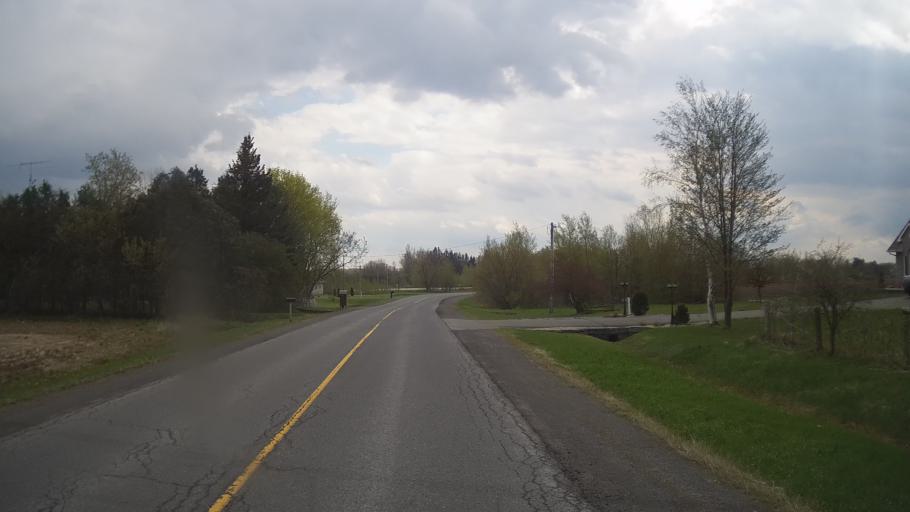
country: CA
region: Ontario
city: Hawkesbury
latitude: 45.5215
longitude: -74.5640
